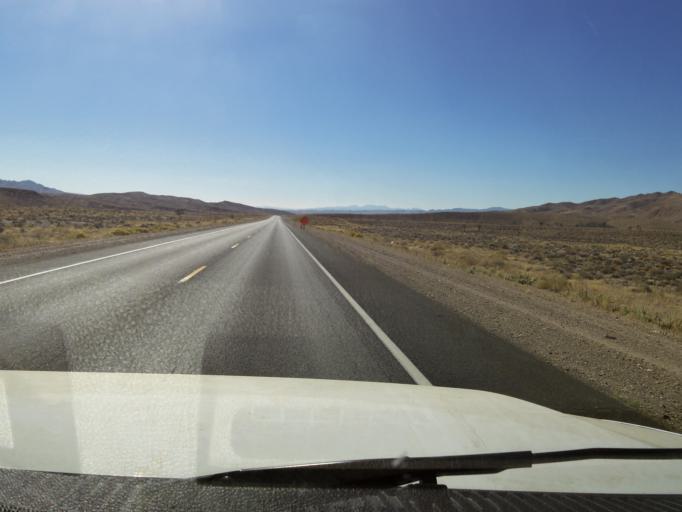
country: US
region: Nevada
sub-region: Esmeralda County
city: Goldfield
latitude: 37.5731
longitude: -117.2023
